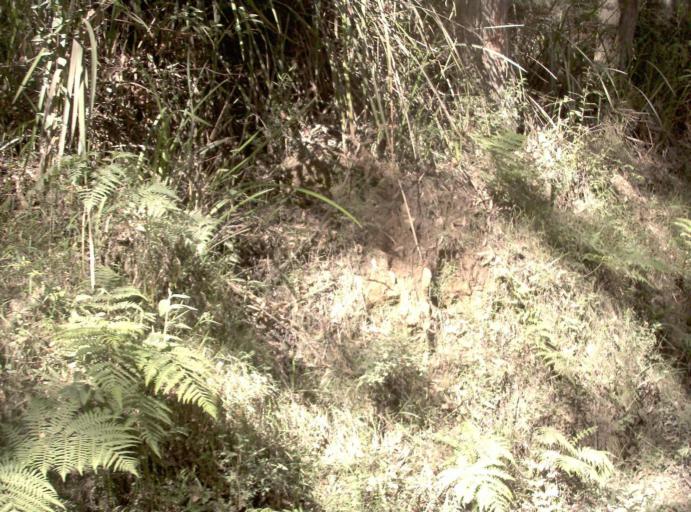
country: AU
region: Victoria
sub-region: Yarra Ranges
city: Millgrove
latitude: -37.7060
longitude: 145.6093
